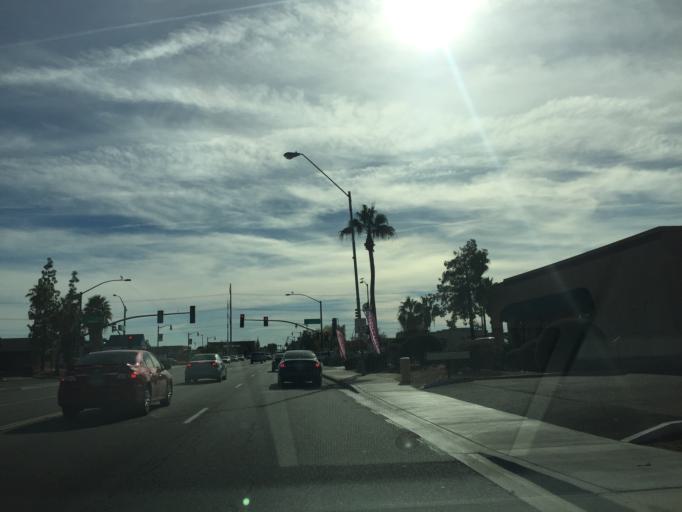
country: US
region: Arizona
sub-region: Maricopa County
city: Gilbert
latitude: 33.3603
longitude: -111.7899
